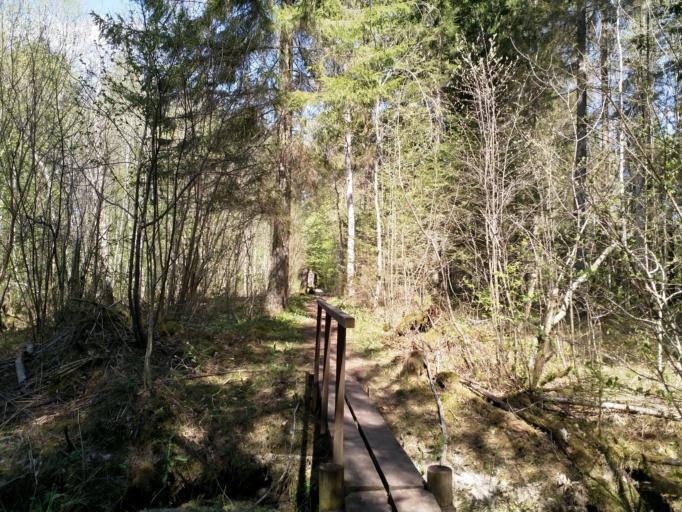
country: LV
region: Kandava
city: Kandava
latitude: 57.0199
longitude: 22.7734
